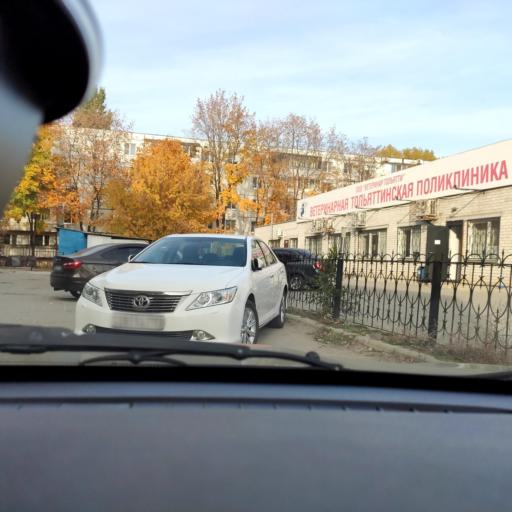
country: RU
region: Samara
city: Tol'yatti
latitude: 53.5278
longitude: 49.3044
